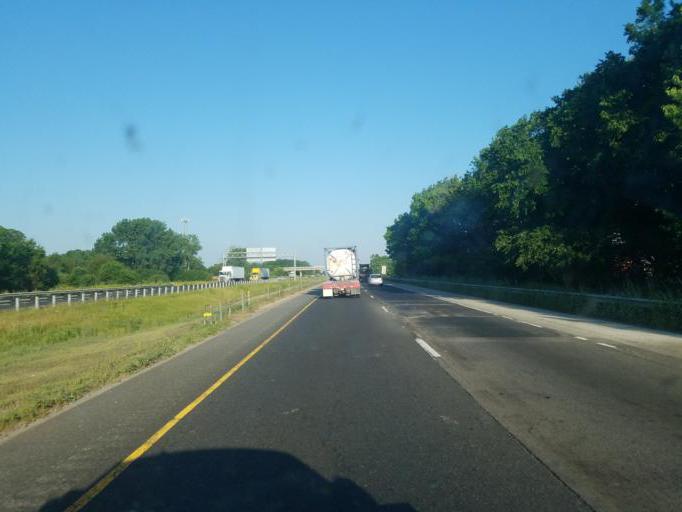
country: US
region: Illinois
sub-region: Will County
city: Shorewood
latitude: 41.4859
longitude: -88.2121
